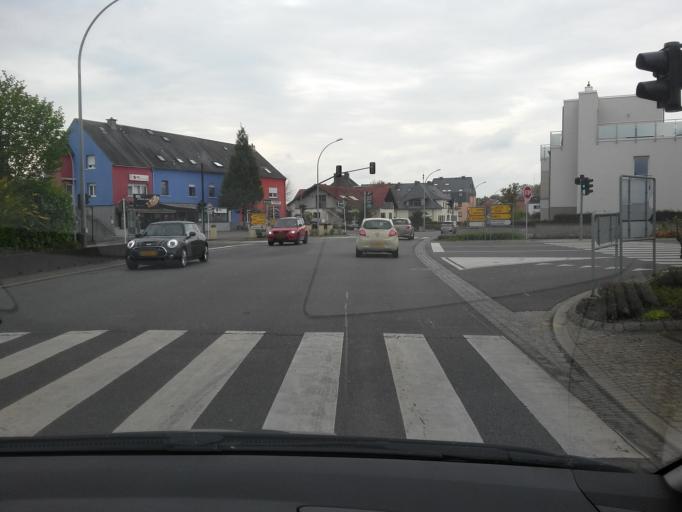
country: LU
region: Luxembourg
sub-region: Canton de Capellen
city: Dippach
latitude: 49.5872
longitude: 5.9858
